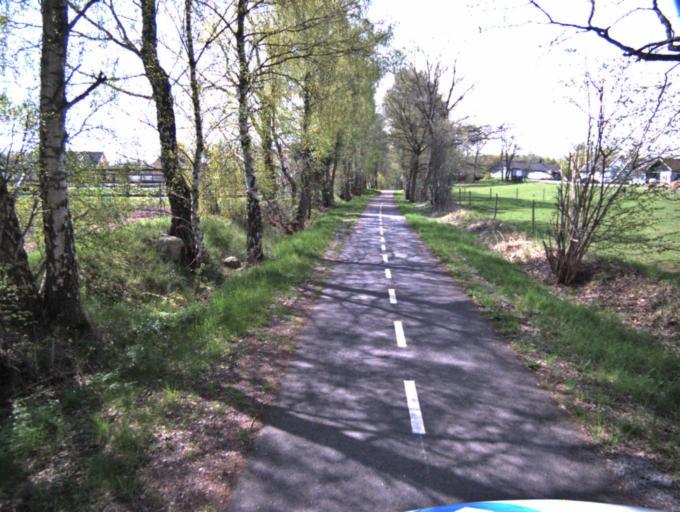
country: SE
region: Skane
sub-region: Kristianstads Kommun
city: Onnestad
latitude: 56.0002
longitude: 14.0436
